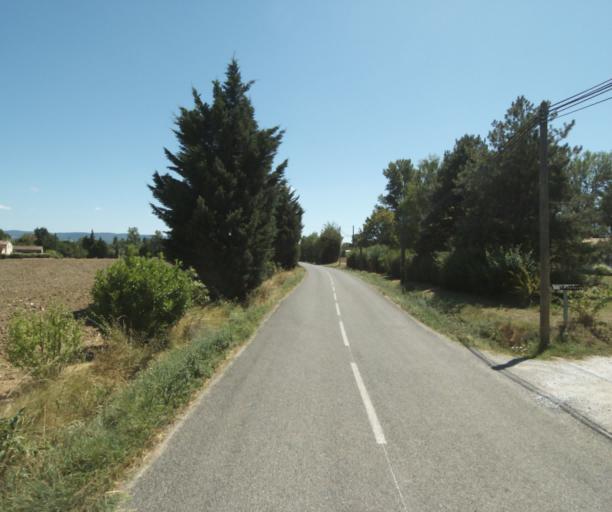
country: FR
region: Midi-Pyrenees
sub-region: Departement de la Haute-Garonne
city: Saint-Felix-Lauragais
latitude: 43.4683
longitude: 1.9281
